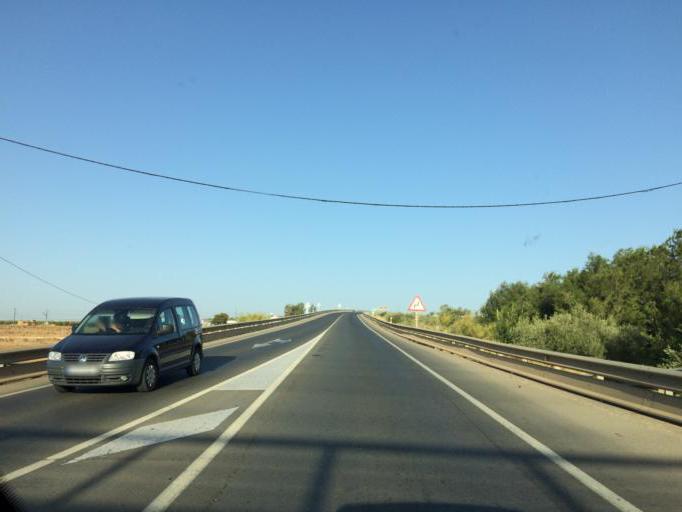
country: ES
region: Andalusia
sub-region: Provincia de Malaga
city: Humilladero
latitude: 37.0620
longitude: -4.7178
